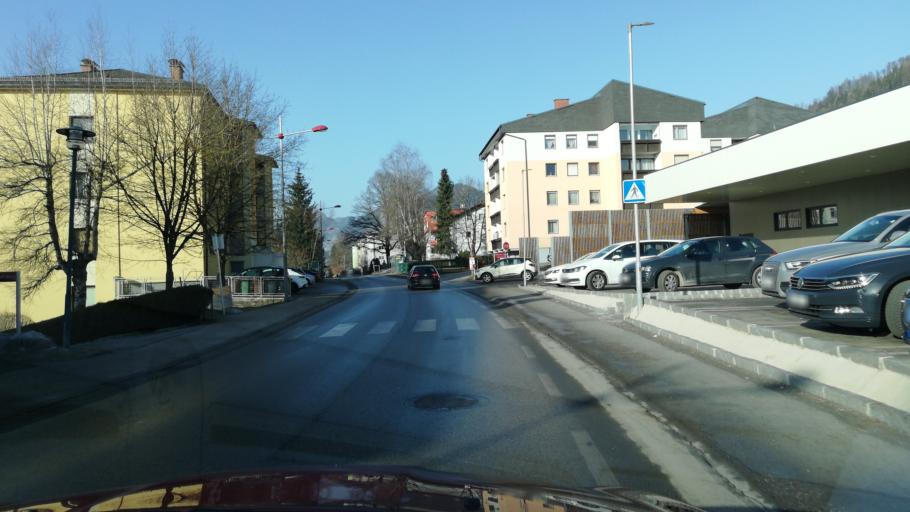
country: AT
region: Styria
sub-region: Politischer Bezirk Liezen
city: Liezen
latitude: 47.5700
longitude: 14.2332
